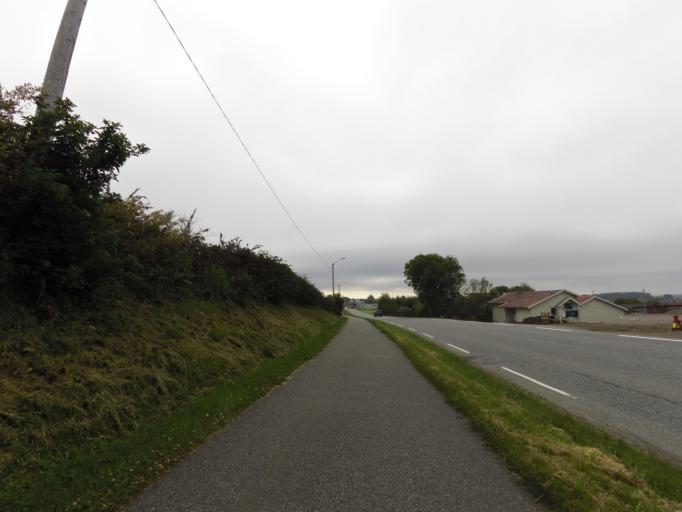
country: NO
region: Rogaland
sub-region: Ha
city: Vigrestad
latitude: 58.5736
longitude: 5.6802
